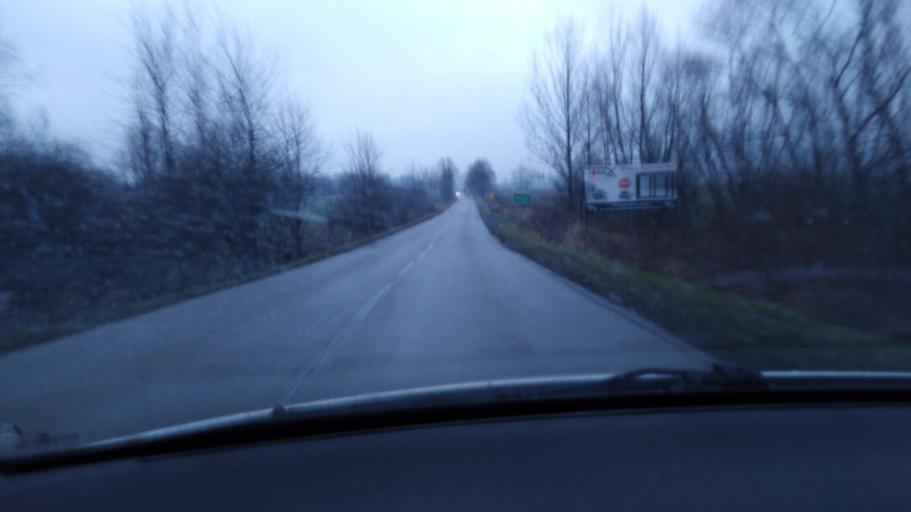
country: PL
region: Silesian Voivodeship
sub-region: Powiat zywiecki
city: Radziechowy
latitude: 49.6353
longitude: 19.1547
